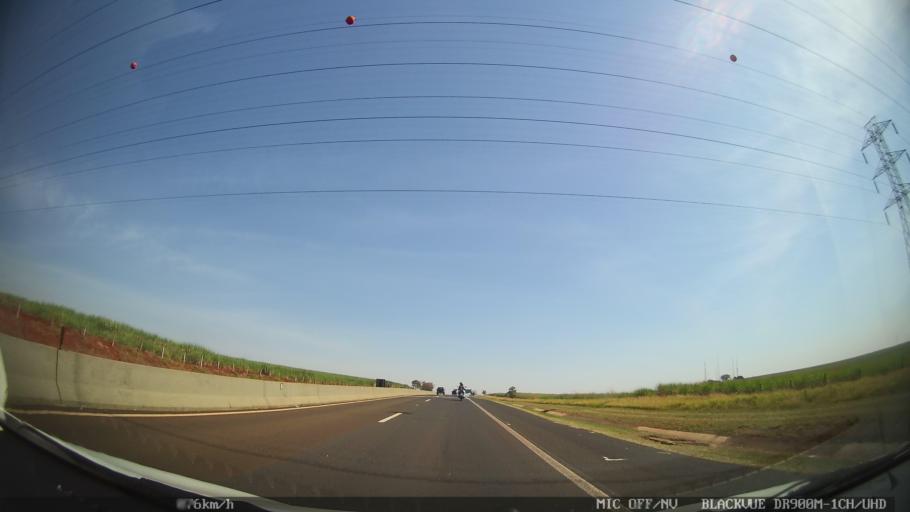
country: BR
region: Sao Paulo
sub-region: Ribeirao Preto
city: Ribeirao Preto
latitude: -21.1661
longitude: -47.8881
